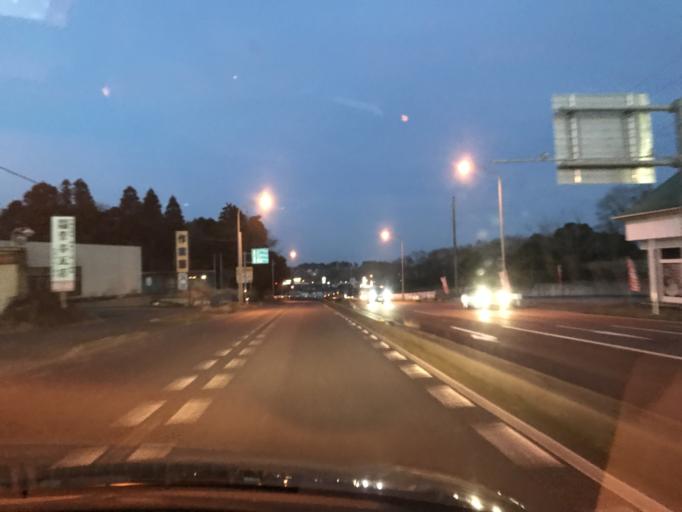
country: JP
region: Chiba
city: Sawara
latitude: 35.8829
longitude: 140.4786
